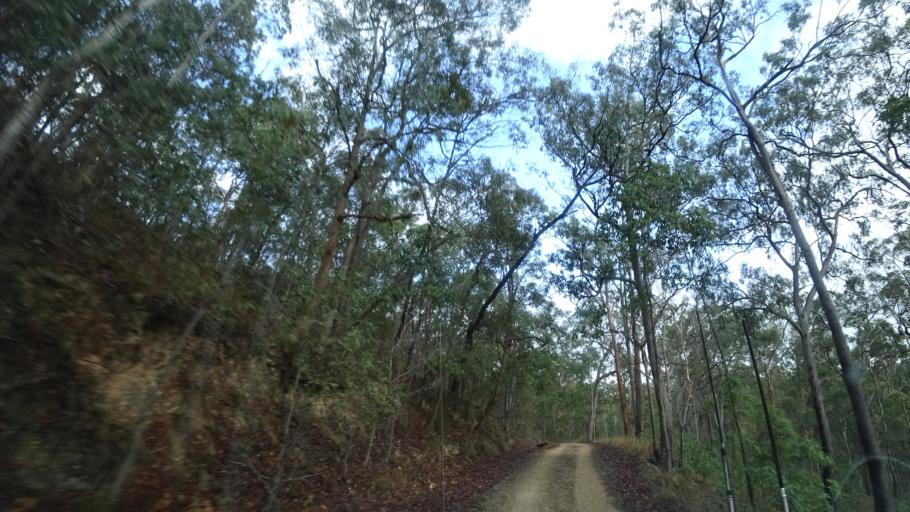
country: AU
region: Queensland
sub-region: Brisbane
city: Kenmore Hills
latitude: -27.4507
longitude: 152.8893
